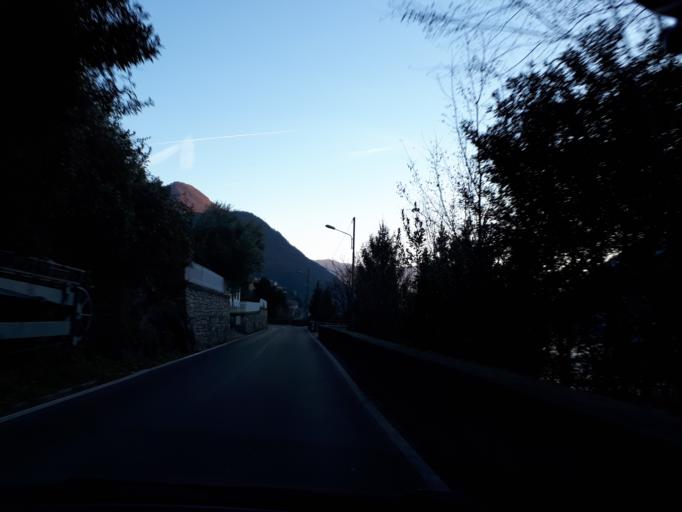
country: IT
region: Lombardy
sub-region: Provincia di Como
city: Nesso
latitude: 45.9220
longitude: 9.1520
